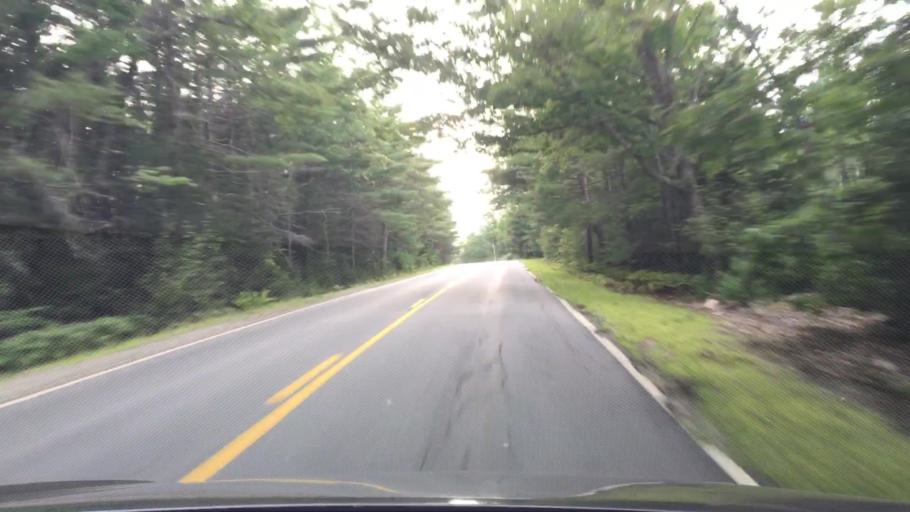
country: US
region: Maine
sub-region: Hancock County
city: Penobscot
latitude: 44.4511
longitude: -68.6878
